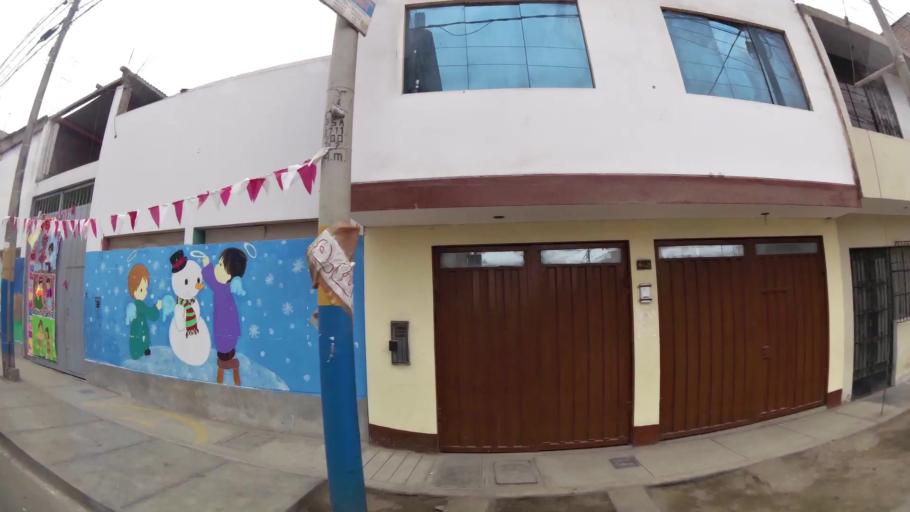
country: PE
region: Lima
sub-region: Lima
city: Surco
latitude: -12.1974
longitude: -76.9663
